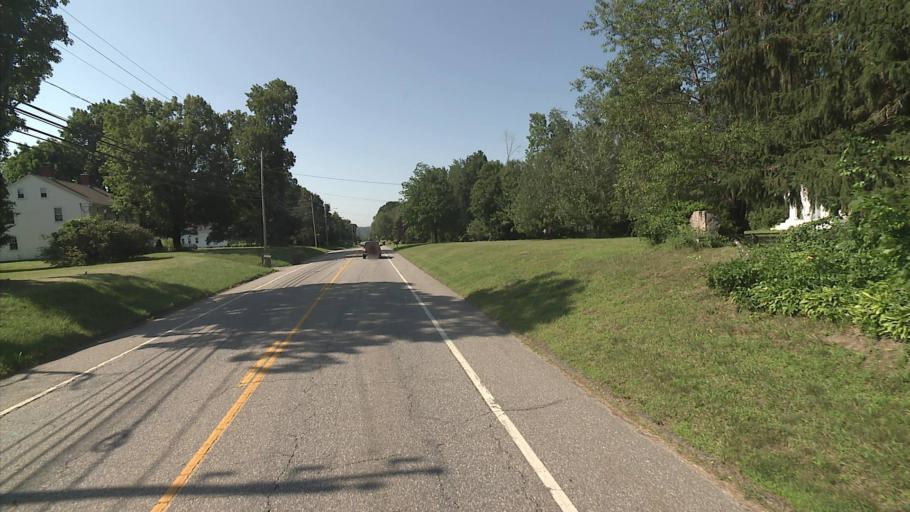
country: US
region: Connecticut
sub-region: Litchfield County
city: Torrington
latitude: 41.8268
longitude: -73.0794
